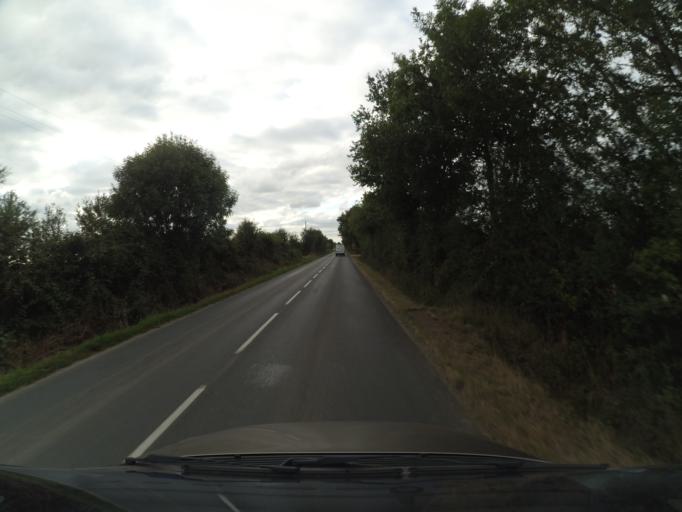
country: FR
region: Pays de la Loire
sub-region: Departement de la Vendee
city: Saint-Andre-Treize-Voies
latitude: 46.9279
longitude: -1.4002
